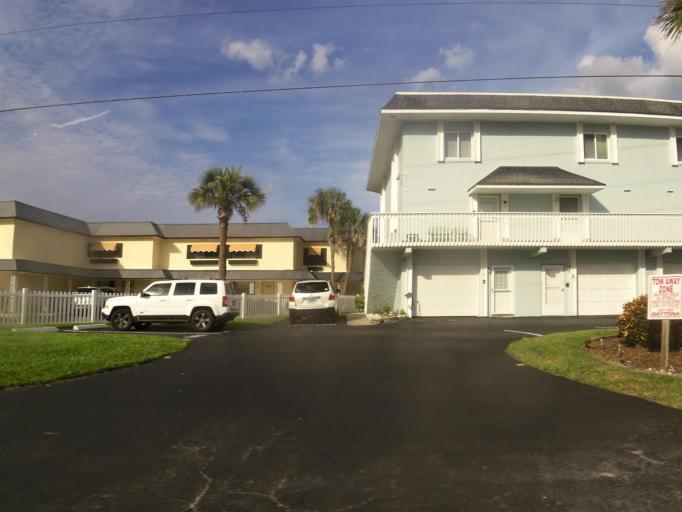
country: US
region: Florida
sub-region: Volusia County
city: Ponce Inlet
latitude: 29.0908
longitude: -80.9311
